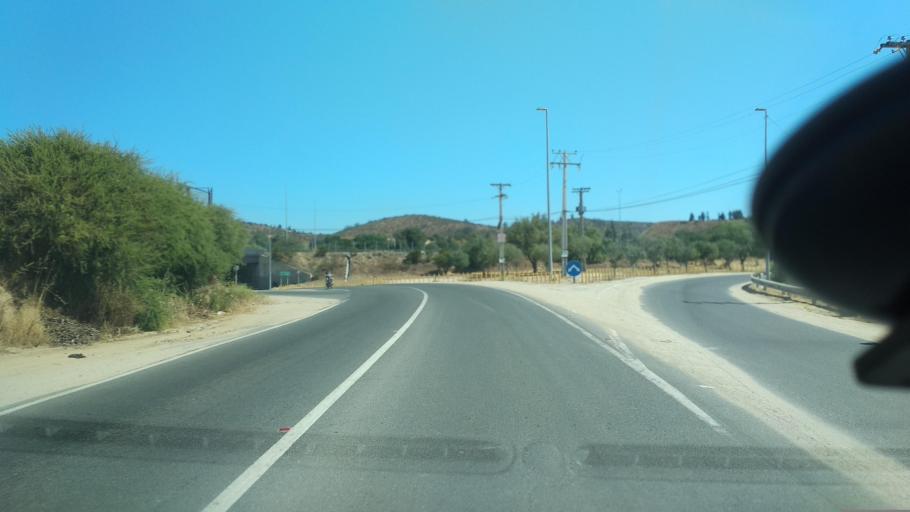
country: CL
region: Valparaiso
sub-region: Provincia de Marga Marga
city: Villa Alemana
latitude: -33.0674
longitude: -71.3713
